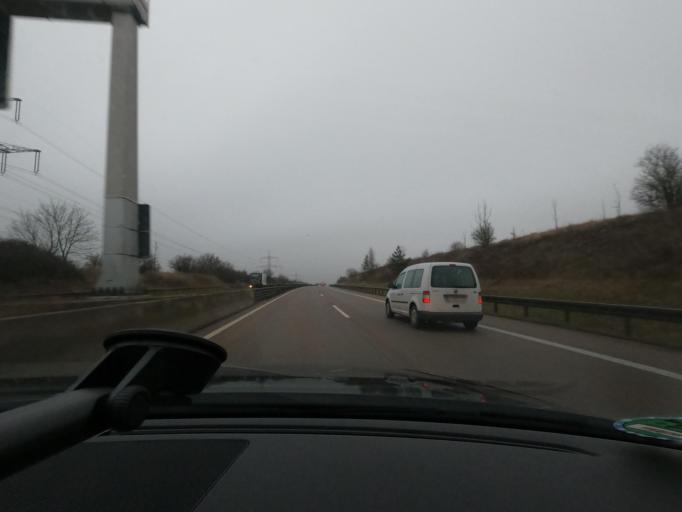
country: DE
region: Thuringia
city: Ichtershausen
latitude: 50.8872
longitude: 10.9797
